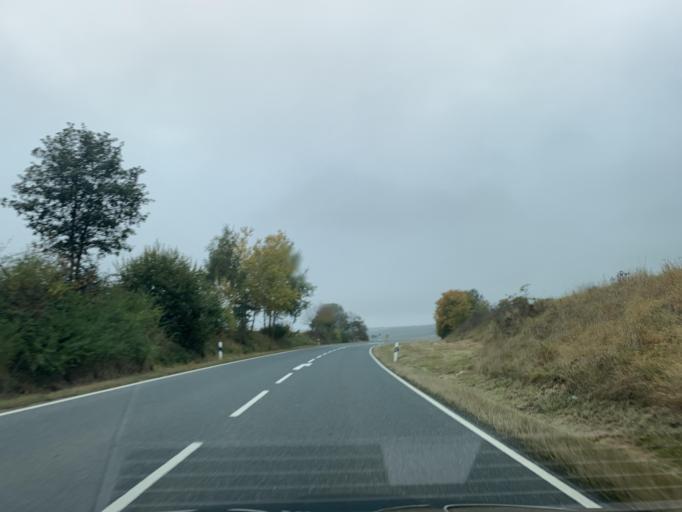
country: DE
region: Bavaria
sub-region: Upper Palatinate
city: Guteneck
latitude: 49.4742
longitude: 12.3028
